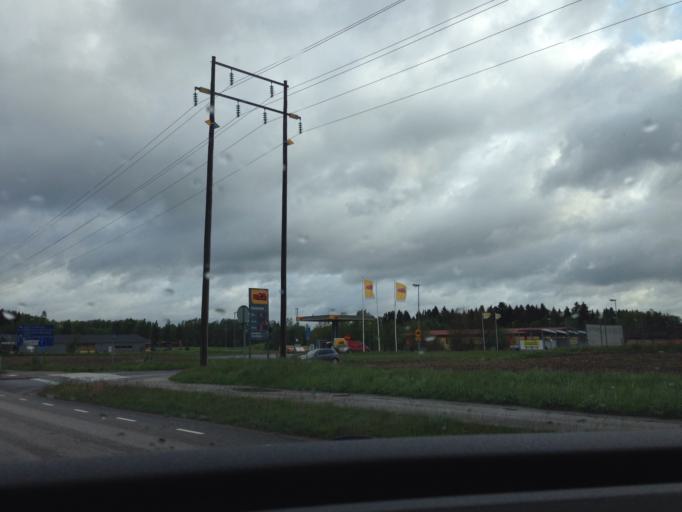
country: SE
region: Vaestra Goetaland
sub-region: Tibro Kommun
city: Tibro
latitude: 58.4182
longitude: 14.1329
